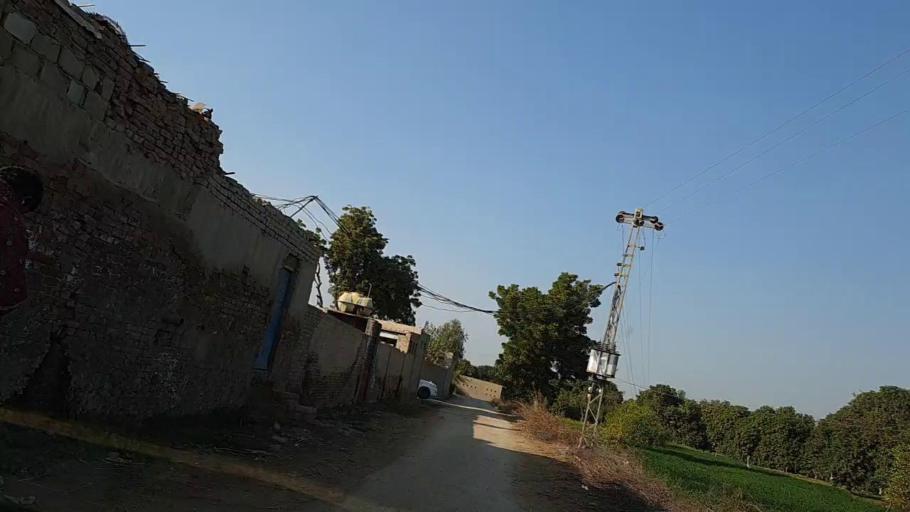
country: PK
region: Sindh
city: Sakrand
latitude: 26.1288
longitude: 68.2214
